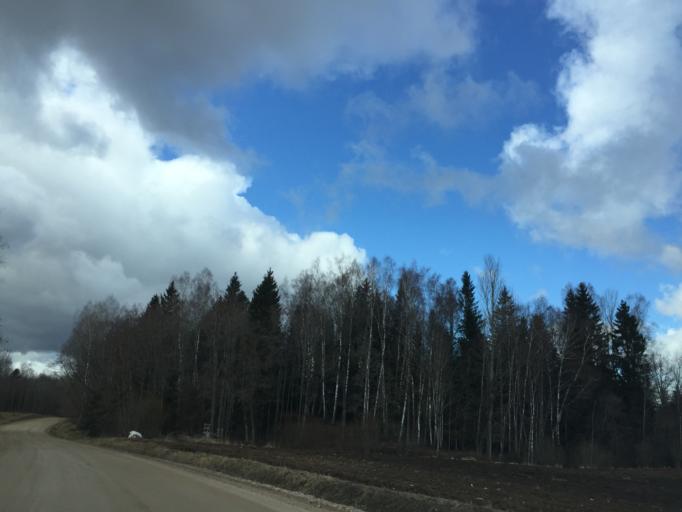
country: LV
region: Akniste
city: Akniste
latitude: 56.1107
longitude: 25.8757
